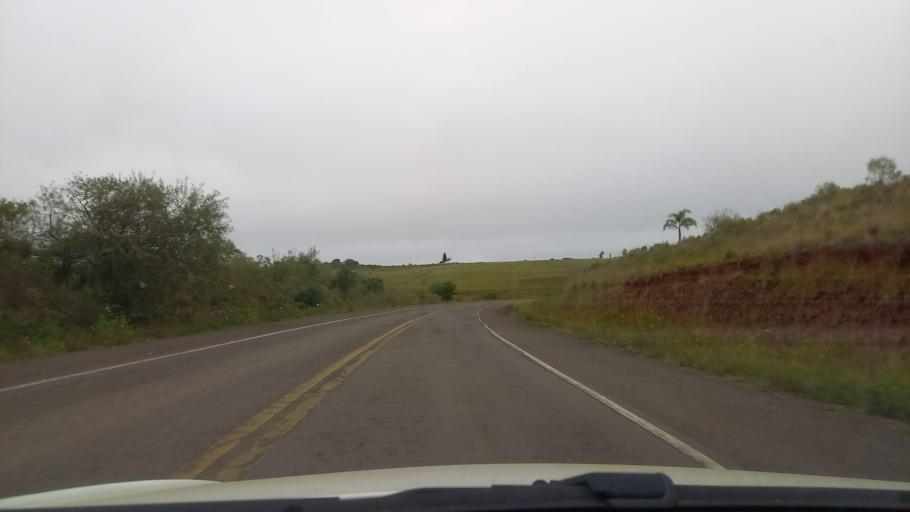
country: BR
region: Rio Grande do Sul
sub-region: Cacequi
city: Cacequi
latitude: -30.0786
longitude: -54.6177
